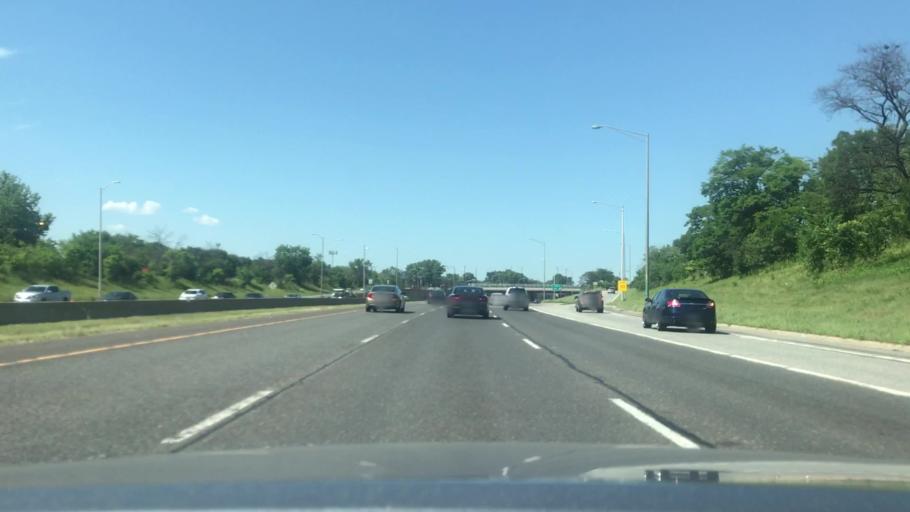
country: US
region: Illinois
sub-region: Cook County
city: Calumet Park
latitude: 41.6855
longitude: -87.6620
